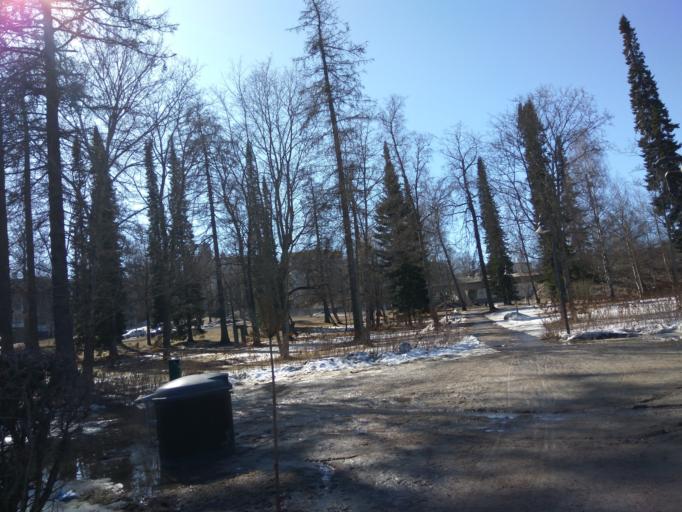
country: FI
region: South Karelia
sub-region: Lappeenranta
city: Lappeenranta
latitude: 61.0625
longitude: 28.1840
